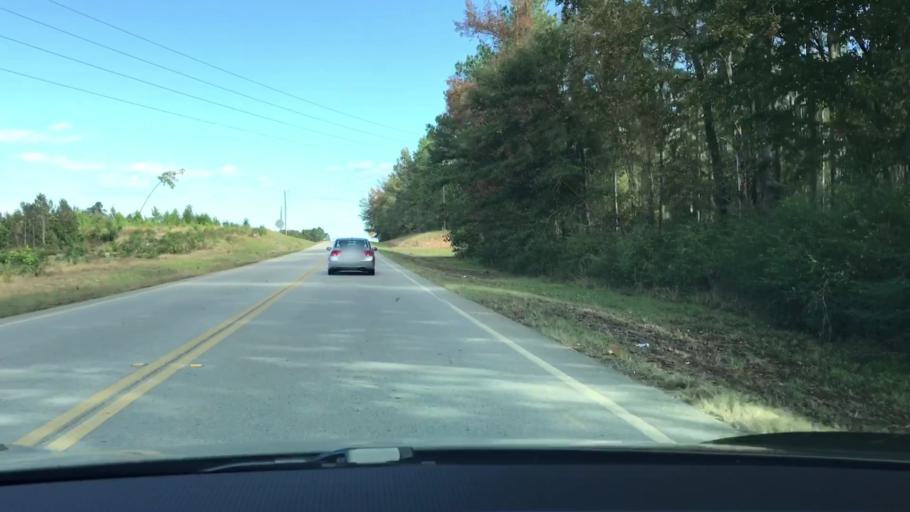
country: US
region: Georgia
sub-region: Jefferson County
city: Wrens
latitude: 33.2253
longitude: -82.4617
